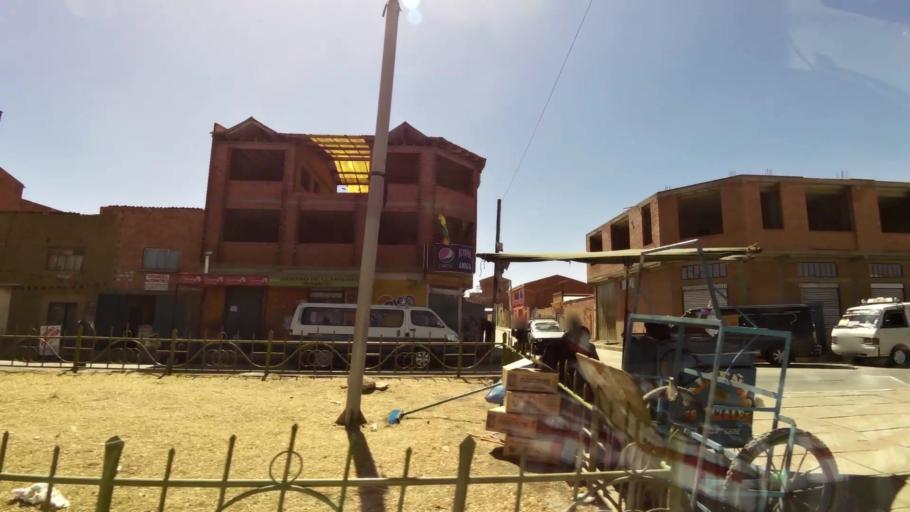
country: BO
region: La Paz
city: La Paz
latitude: -16.5062
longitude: -68.2187
